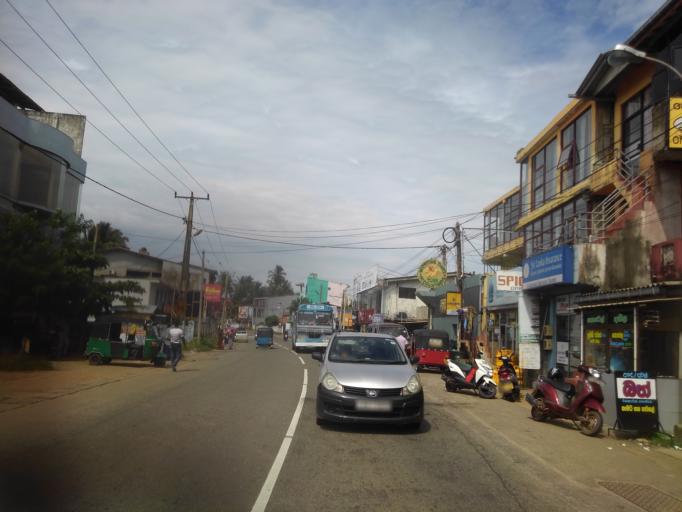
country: LK
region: Southern
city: Hikkaduwa
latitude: 6.1424
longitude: 80.0998
